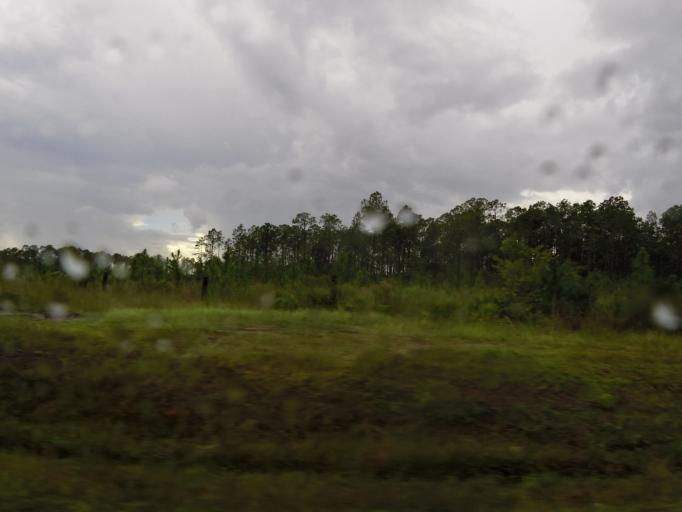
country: US
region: Florida
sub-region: Duval County
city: Baldwin
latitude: 30.4850
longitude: -81.9990
